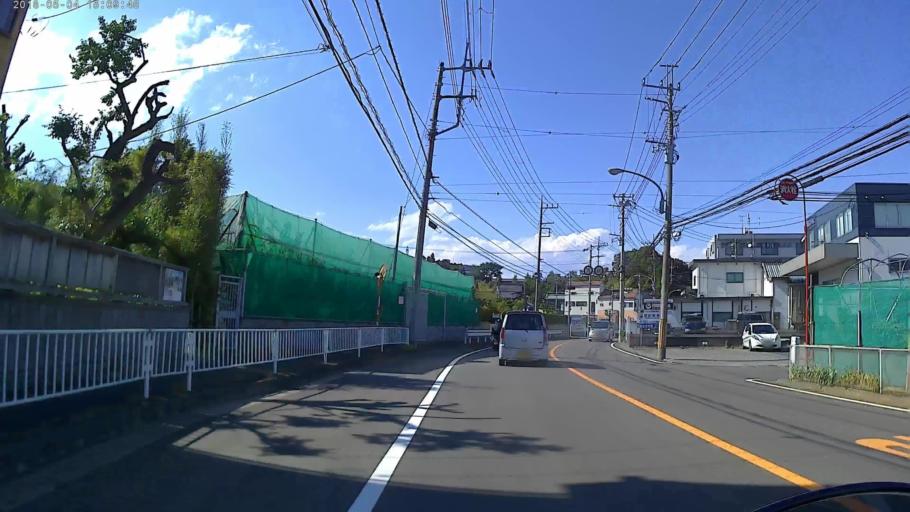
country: JP
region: Kanagawa
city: Yokohama
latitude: 35.5195
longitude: 139.6095
